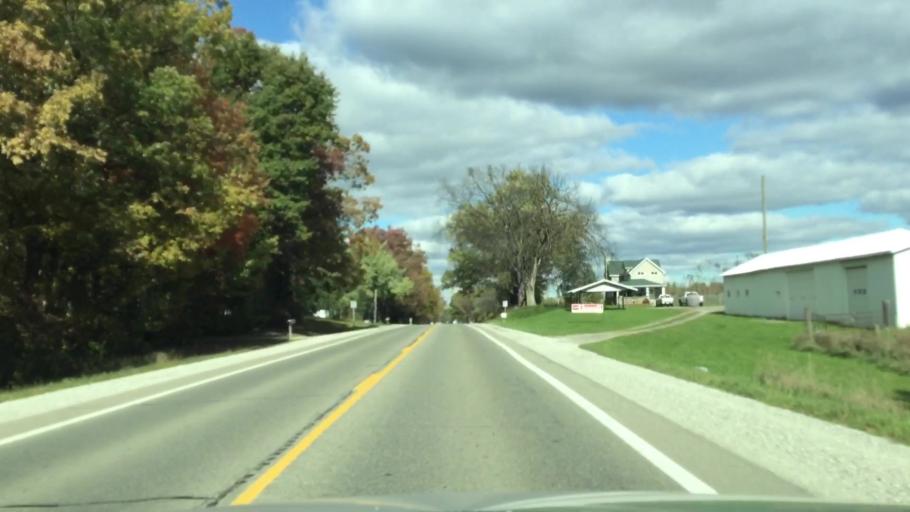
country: US
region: Michigan
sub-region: Lapeer County
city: Barnes Lake-Millers Lake
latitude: 43.1496
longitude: -83.3112
